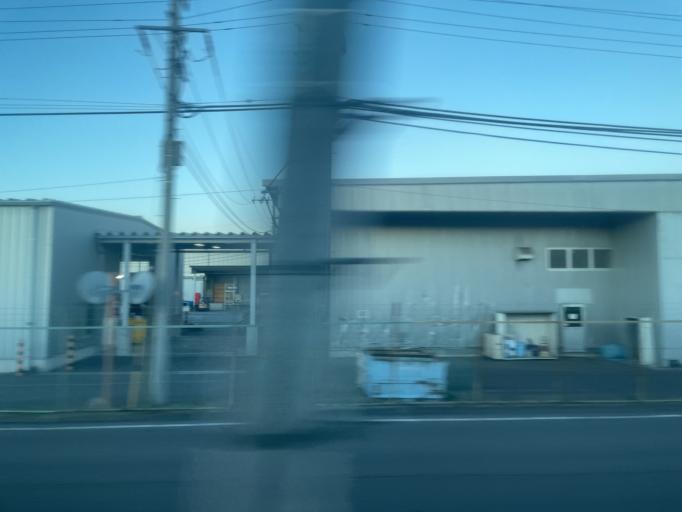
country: JP
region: Saitama
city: Fukayacho
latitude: 36.1842
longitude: 139.3072
